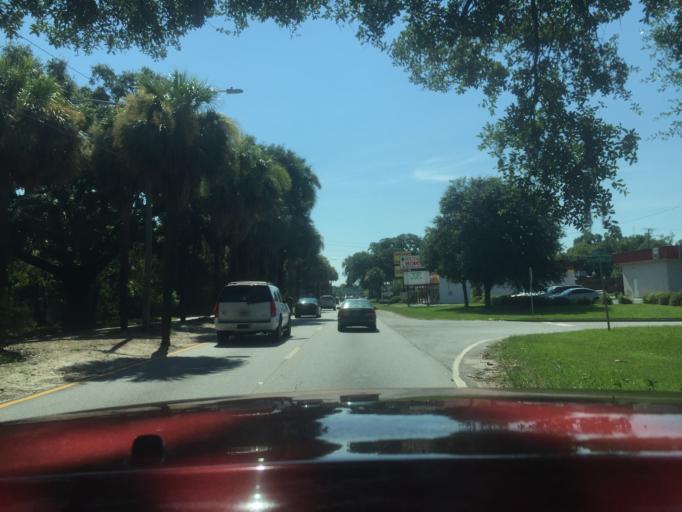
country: US
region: Georgia
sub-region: Chatham County
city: Thunderbolt
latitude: 32.0454
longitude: -81.0755
